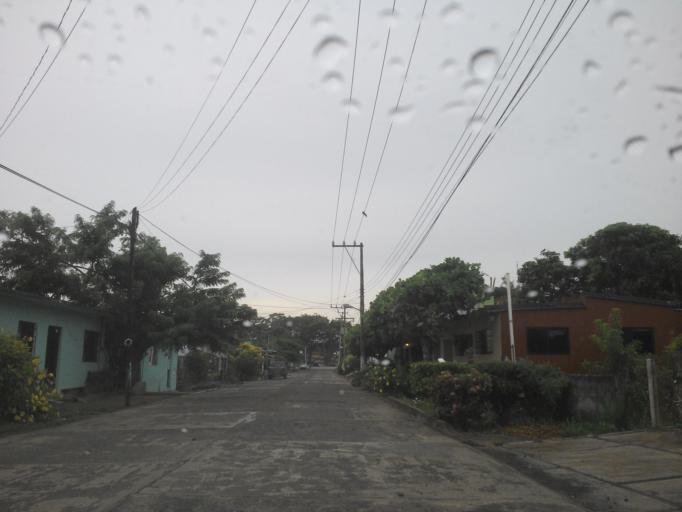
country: MX
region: Veracruz
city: Nautla
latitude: 20.2107
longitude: -96.7782
